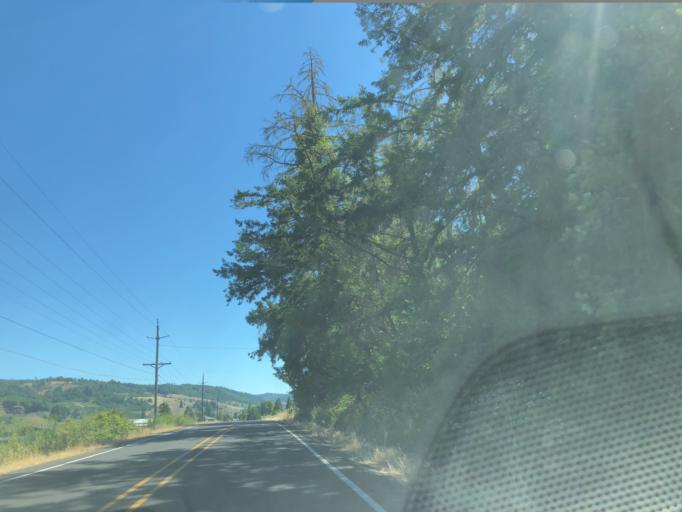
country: US
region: Oregon
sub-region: Douglas County
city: Yoncalla
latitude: 43.5770
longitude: -123.2809
